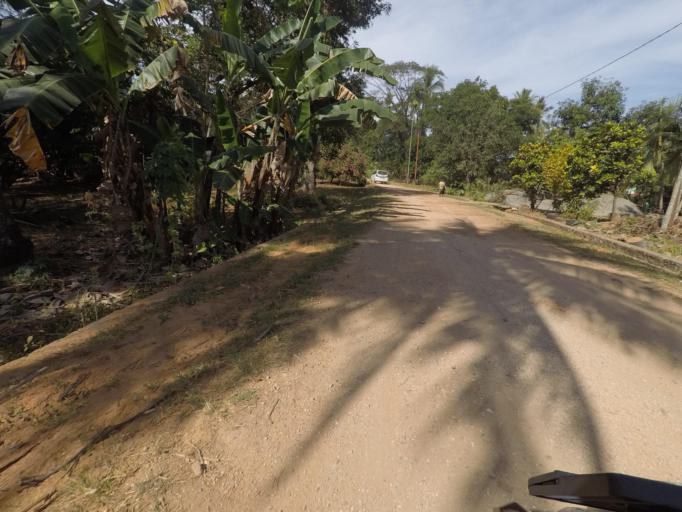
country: TL
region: Bobonaro
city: Maliana
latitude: -8.9613
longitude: 125.2179
